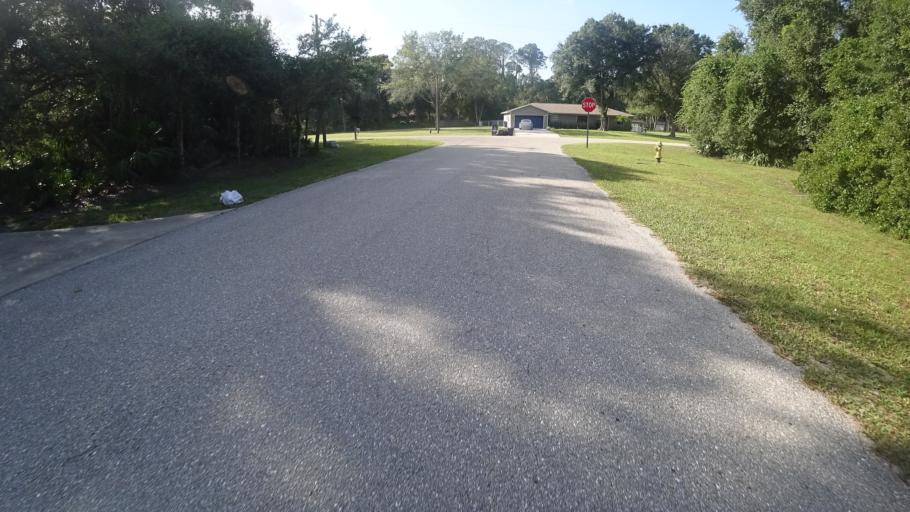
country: US
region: Florida
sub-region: Sarasota County
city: The Meadows
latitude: 27.4386
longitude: -82.4385
